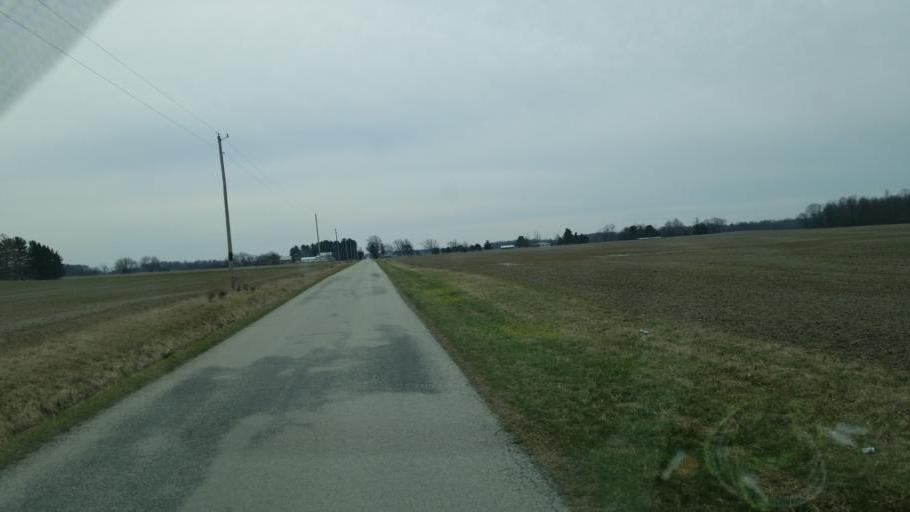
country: US
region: Ohio
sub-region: Huron County
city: Norwalk
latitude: 41.1386
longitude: -82.5649
